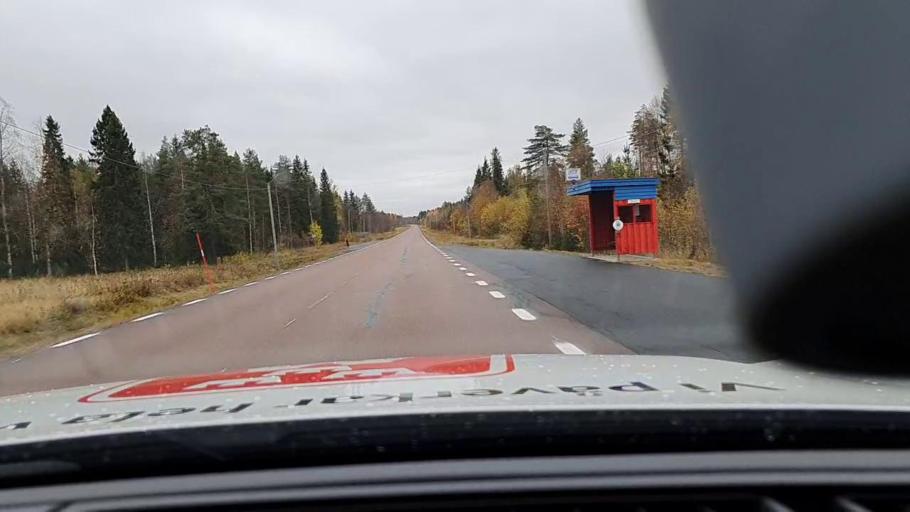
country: FI
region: Lapland
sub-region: Kemi-Tornio
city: Tornio
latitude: 66.0873
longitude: 23.9252
